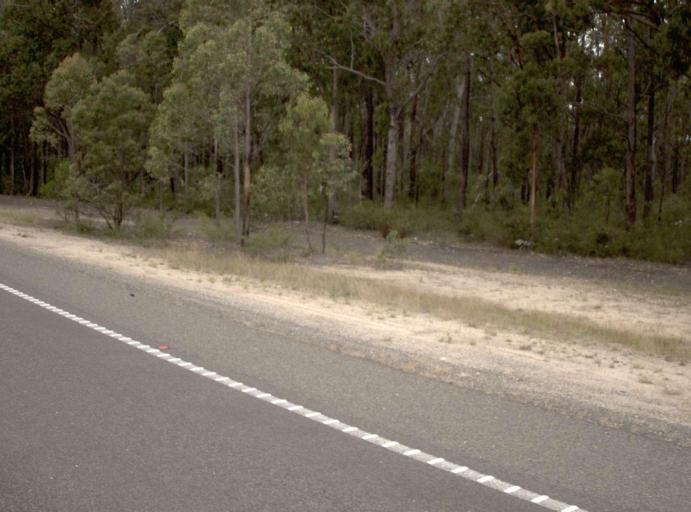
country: AU
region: Victoria
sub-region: East Gippsland
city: Lakes Entrance
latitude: -37.7235
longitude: 147.9547
